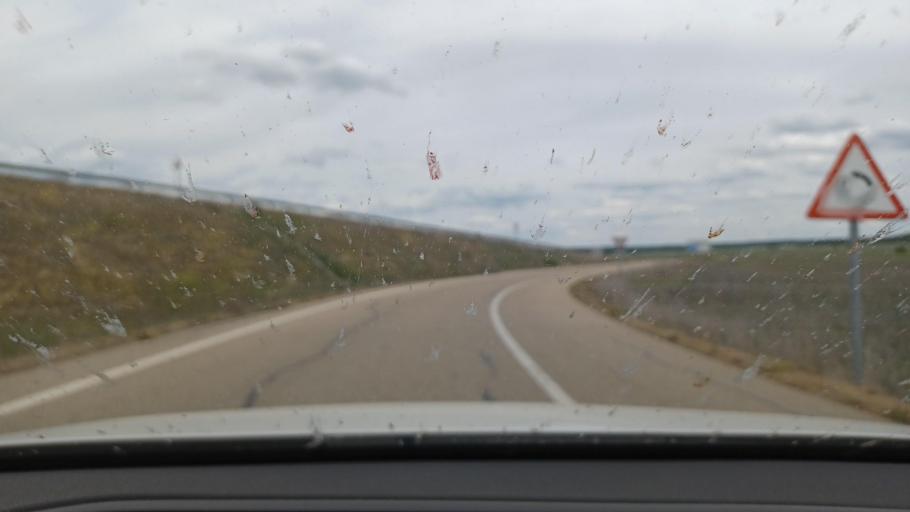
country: ES
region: Castille and Leon
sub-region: Provincia de Valladolid
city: Portillo
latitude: 41.4888
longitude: -4.6137
